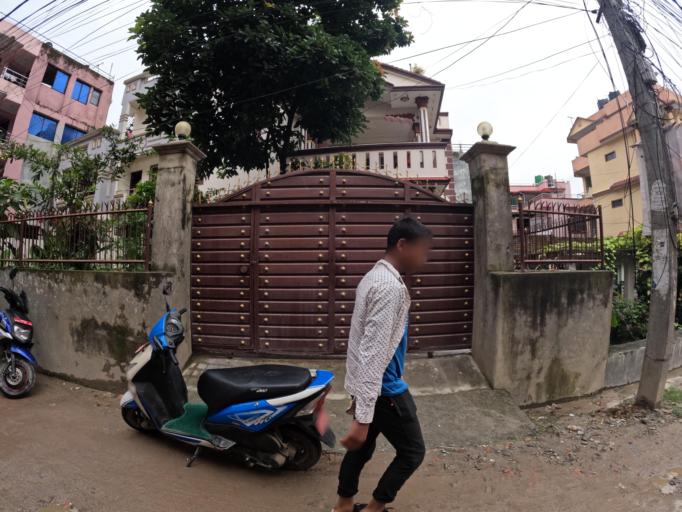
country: NP
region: Central Region
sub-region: Bagmati Zone
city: Kathmandu
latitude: 27.7552
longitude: 85.3237
